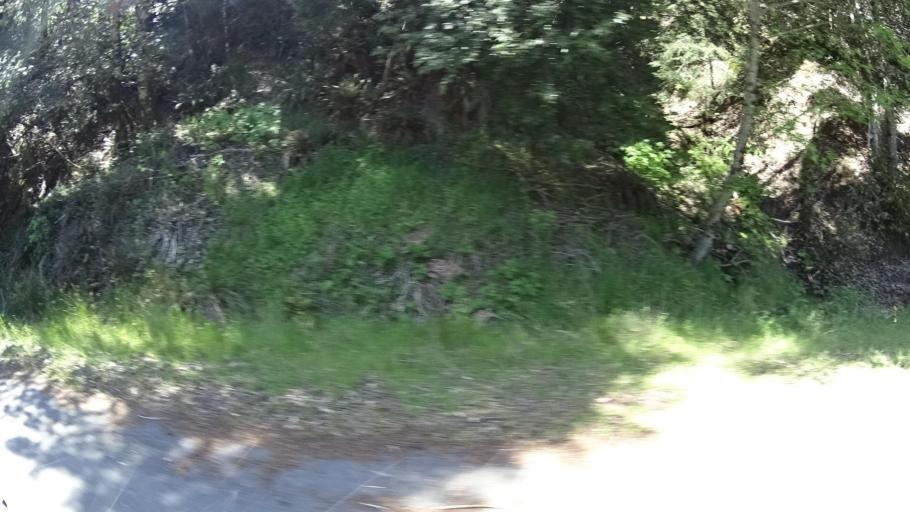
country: US
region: California
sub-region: Humboldt County
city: Rio Dell
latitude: 40.3193
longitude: -124.0620
